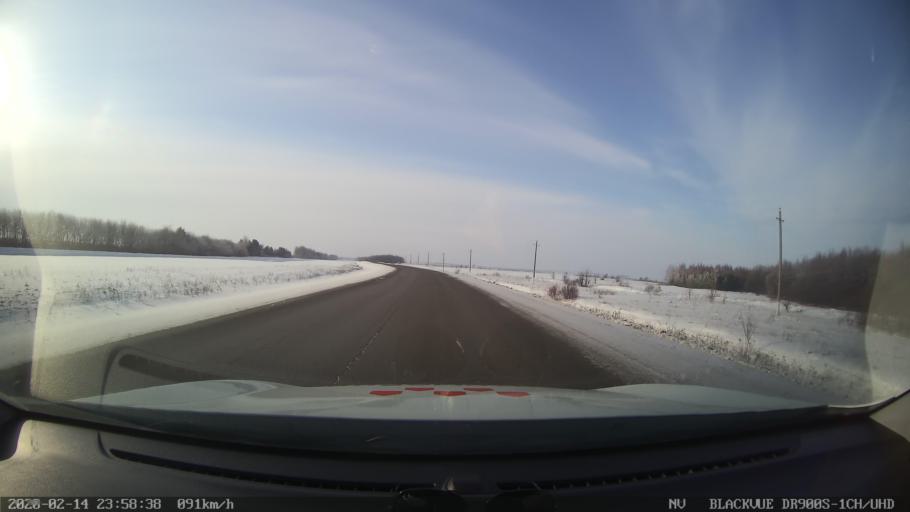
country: RU
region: Tatarstan
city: Kuybyshevskiy Zaton
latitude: 55.3417
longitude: 49.0835
